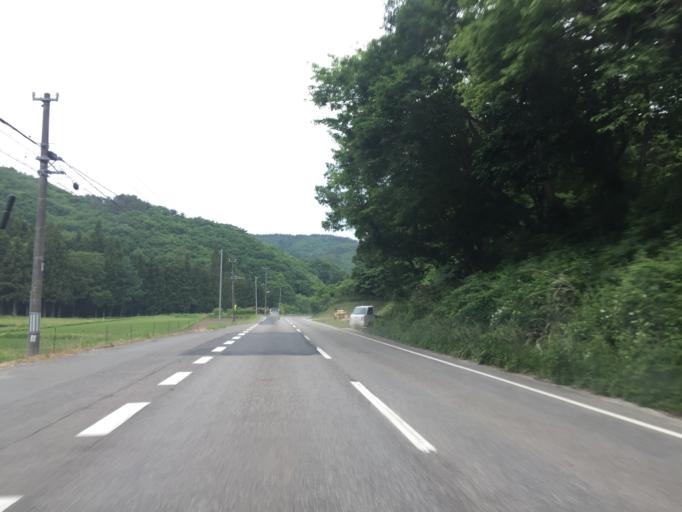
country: JP
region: Fukushima
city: Namie
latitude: 37.4131
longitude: 140.8295
